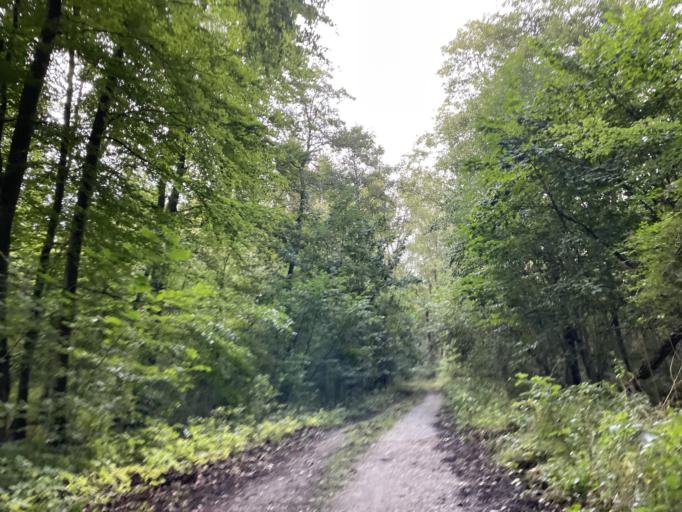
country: DE
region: Lower Saxony
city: Lueneburg
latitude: 53.2275
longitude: 10.4263
